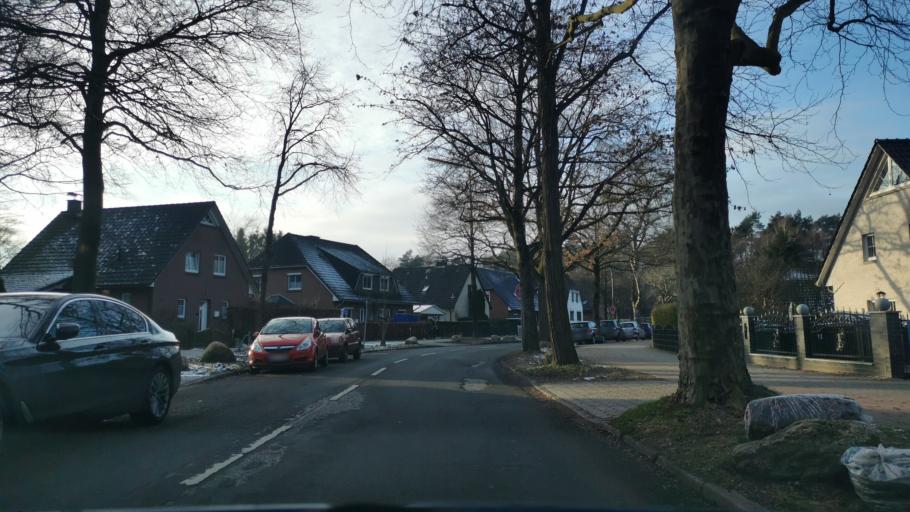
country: DE
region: Hamburg
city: Harburg
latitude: 53.4503
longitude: 9.9249
